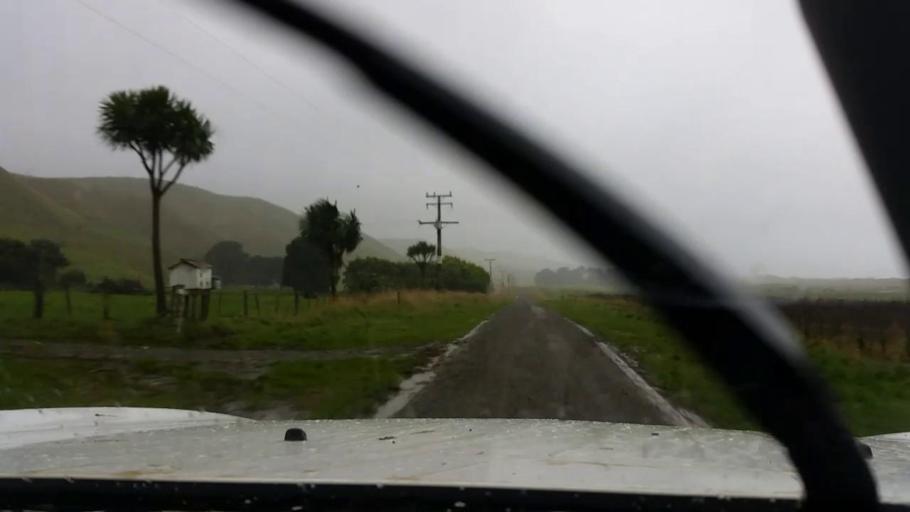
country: NZ
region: Wellington
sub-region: Masterton District
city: Masterton
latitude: -41.2576
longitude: 175.9033
